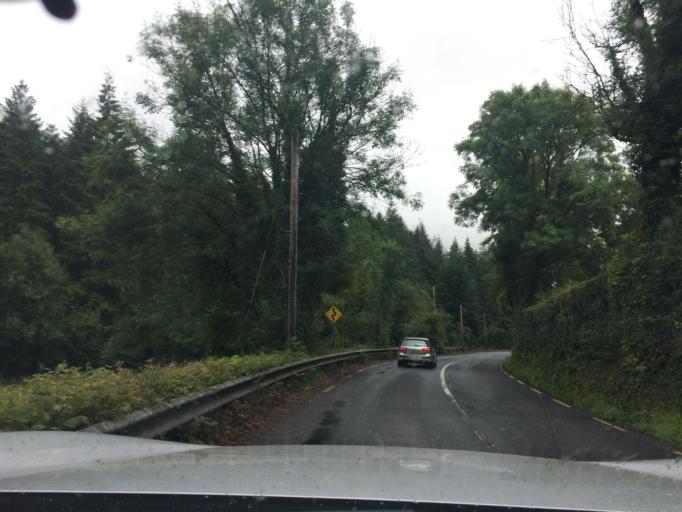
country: IE
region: Munster
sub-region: South Tipperary
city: Cluain Meala
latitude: 52.2659
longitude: -7.7098
